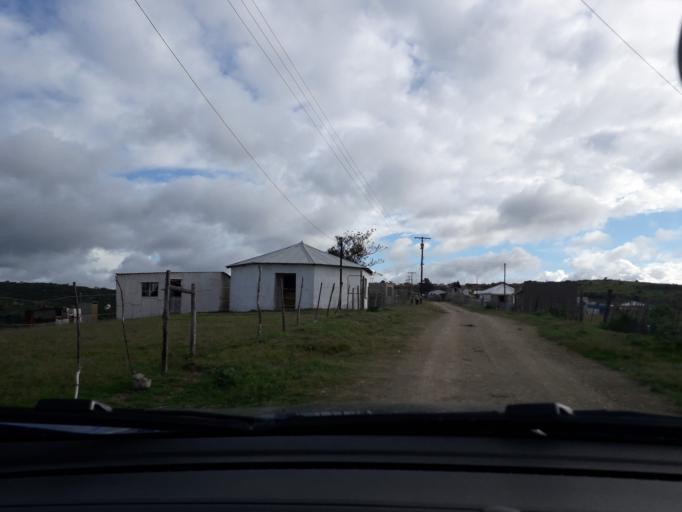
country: ZA
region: Eastern Cape
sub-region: Buffalo City Metropolitan Municipality
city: East London
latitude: -32.8040
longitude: 27.9642
